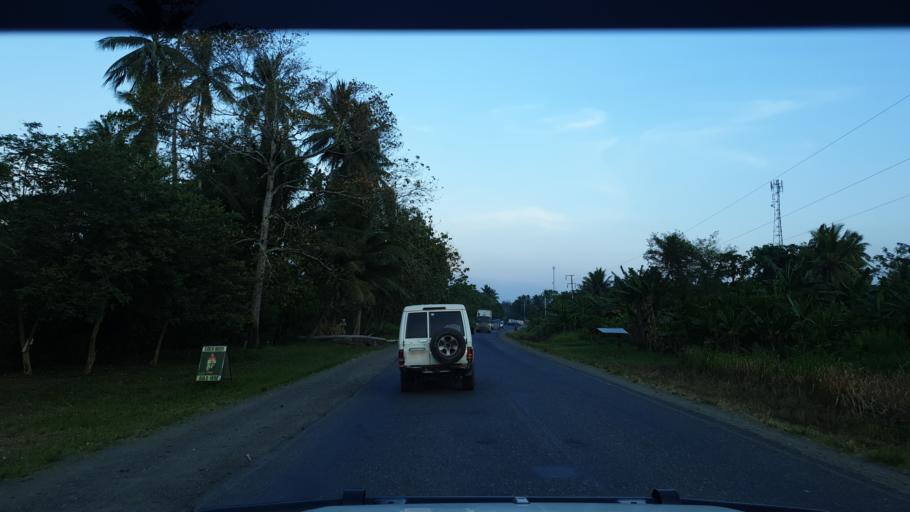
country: PG
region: Morobe
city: Lae
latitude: -6.5963
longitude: 146.7915
